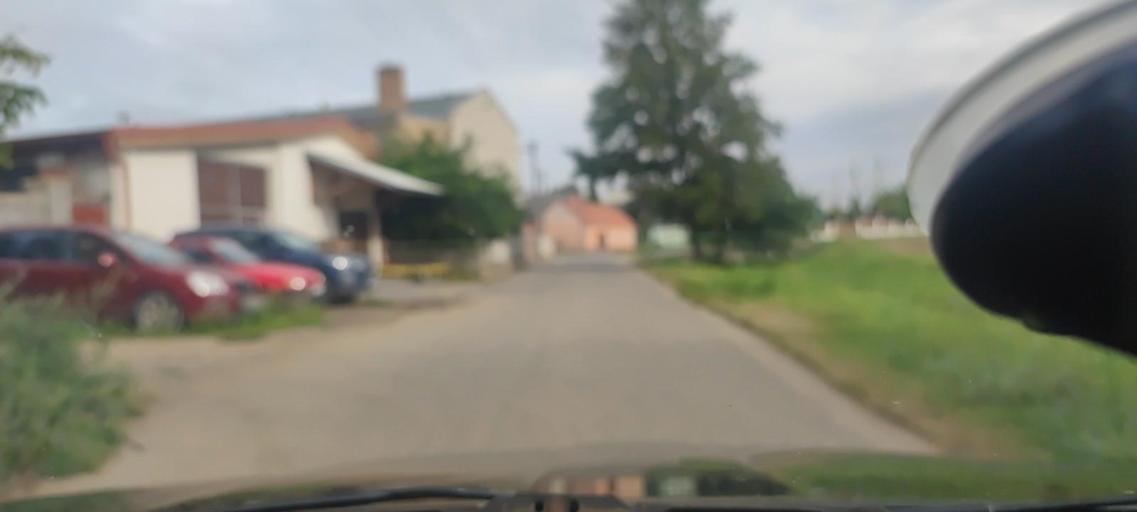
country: CZ
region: South Moravian
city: Hosteradice
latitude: 48.9503
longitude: 16.2608
